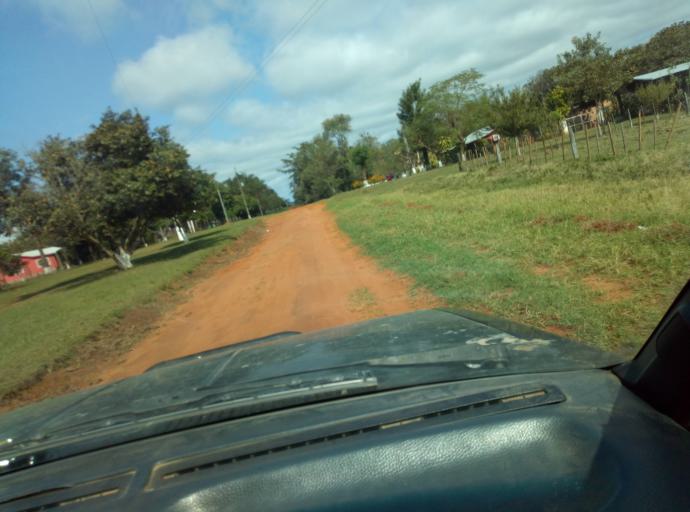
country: PY
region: Caaguazu
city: Doctor Cecilio Baez
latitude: -25.1540
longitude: -56.2913
